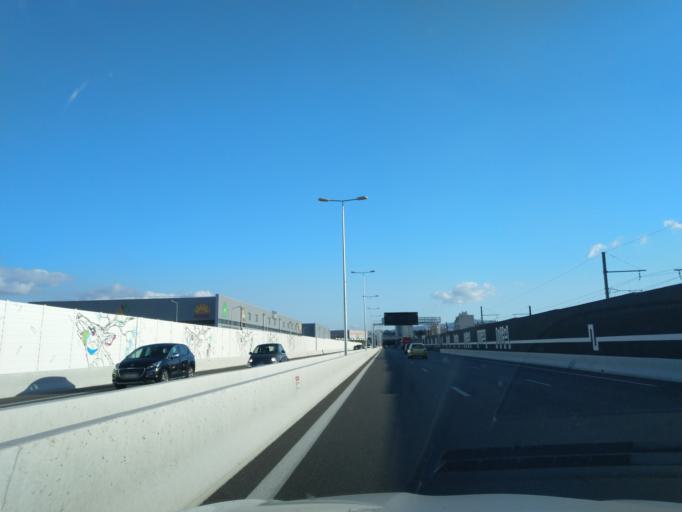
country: FR
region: Provence-Alpes-Cote d'Azur
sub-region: Departement des Bouches-du-Rhone
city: Marseille 14
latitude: 43.3357
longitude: 5.3811
